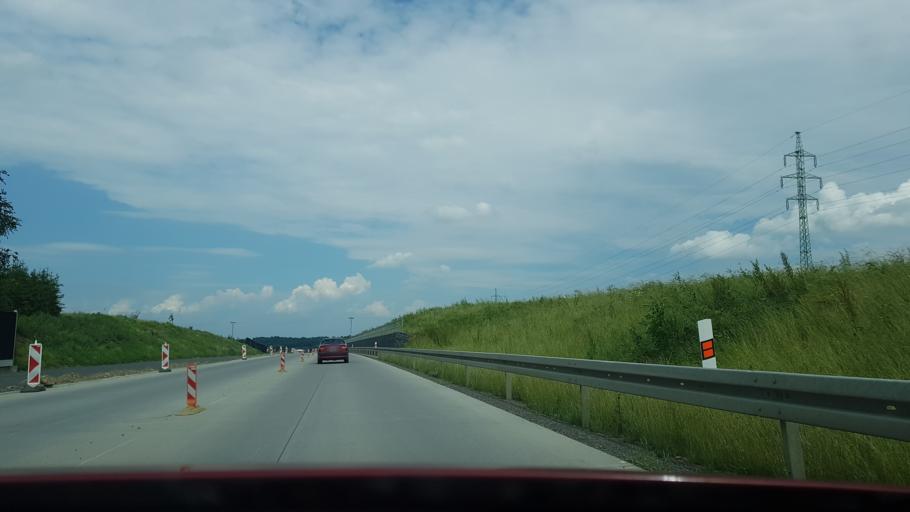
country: CZ
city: Rybi
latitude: 49.6235
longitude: 18.0786
